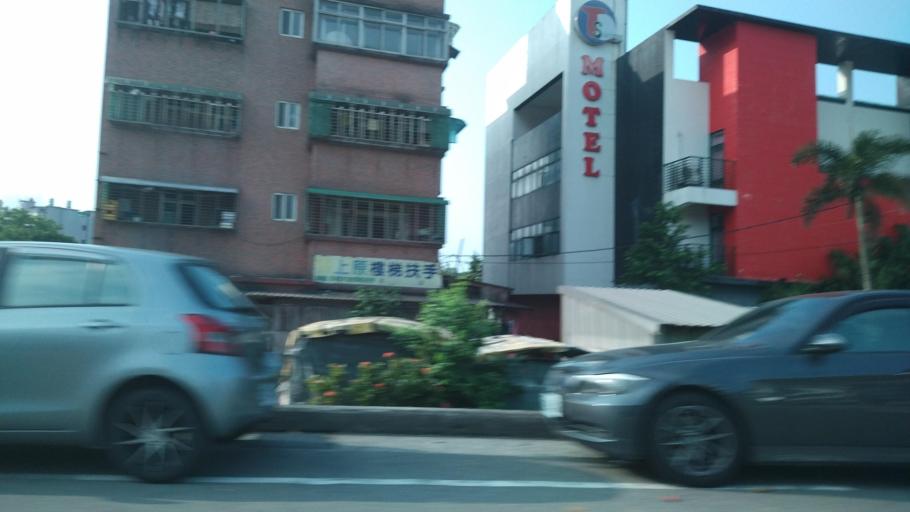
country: TW
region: Taiwan
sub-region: Keelung
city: Keelung
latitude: 25.2176
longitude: 121.6372
